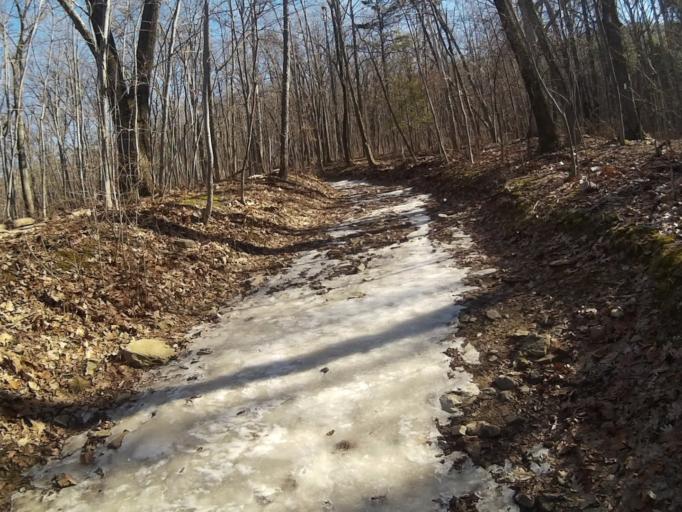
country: US
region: Pennsylvania
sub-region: Centre County
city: Lemont
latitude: 40.8114
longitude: -77.8063
